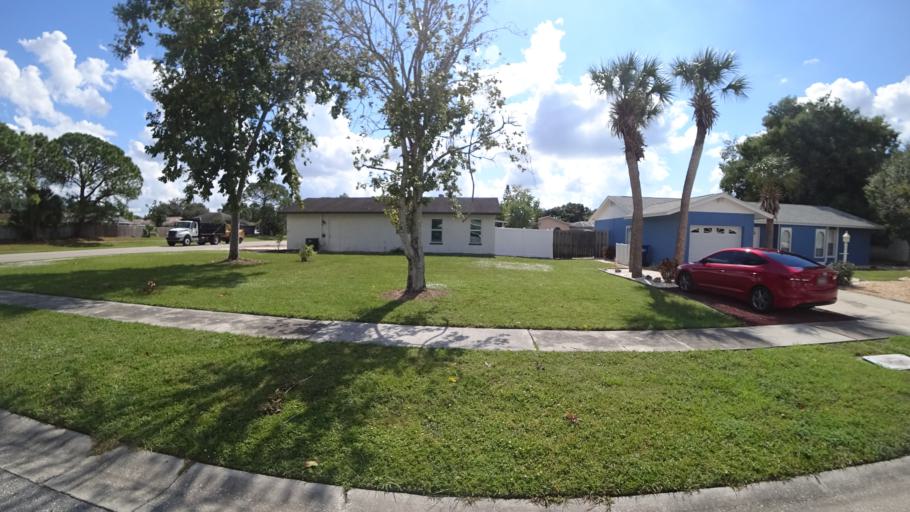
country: US
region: Florida
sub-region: Manatee County
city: Whitfield
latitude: 27.4142
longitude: -82.5553
